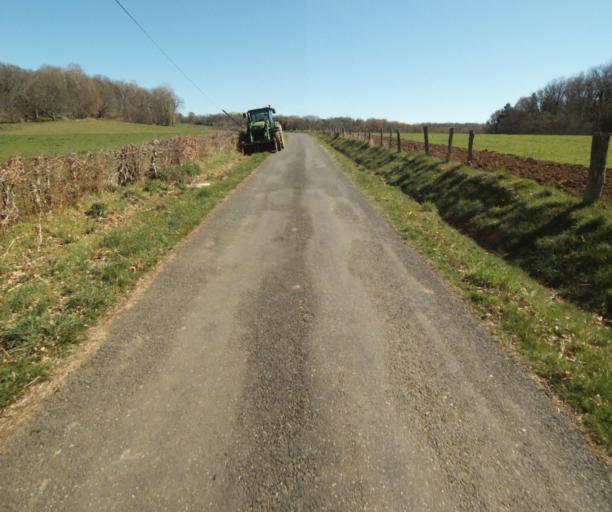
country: FR
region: Limousin
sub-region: Departement de la Correze
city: Chamboulive
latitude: 45.4192
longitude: 1.7313
